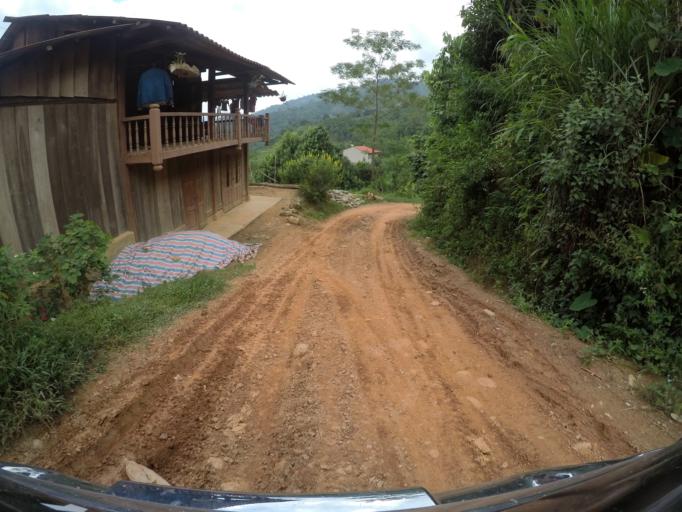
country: VN
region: Yen Bai
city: Son Thinh
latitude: 21.6813
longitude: 104.5783
